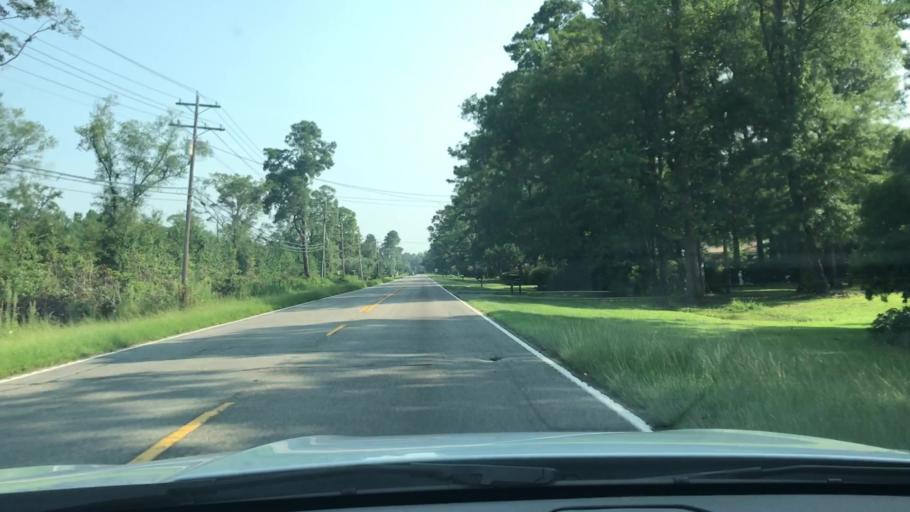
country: US
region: South Carolina
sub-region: Georgetown County
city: Georgetown
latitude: 33.4288
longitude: -79.2794
